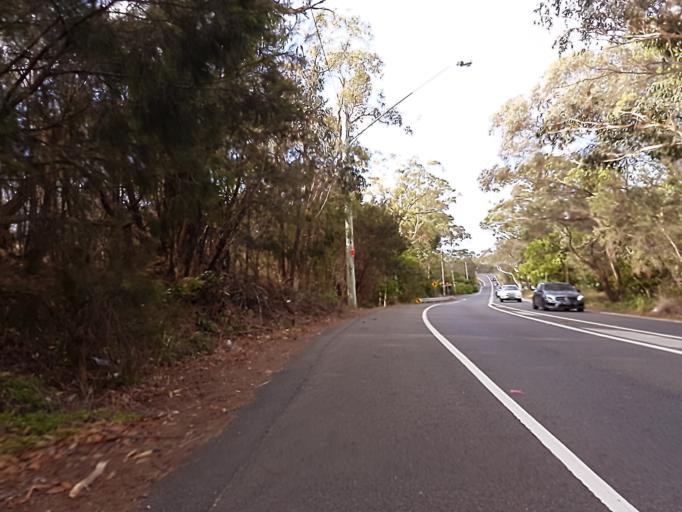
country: AU
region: New South Wales
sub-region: Warringah
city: Killarney Heights
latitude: -33.7817
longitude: 151.2377
